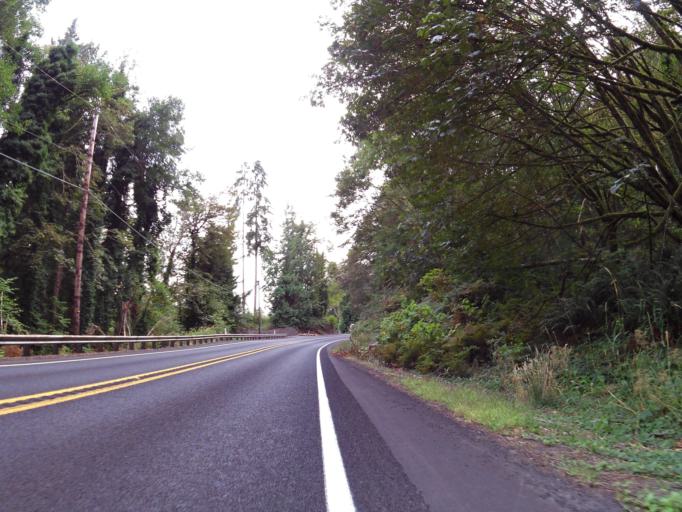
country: US
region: Oregon
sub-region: Columbia County
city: Clatskanie
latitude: 46.1715
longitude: -123.2340
